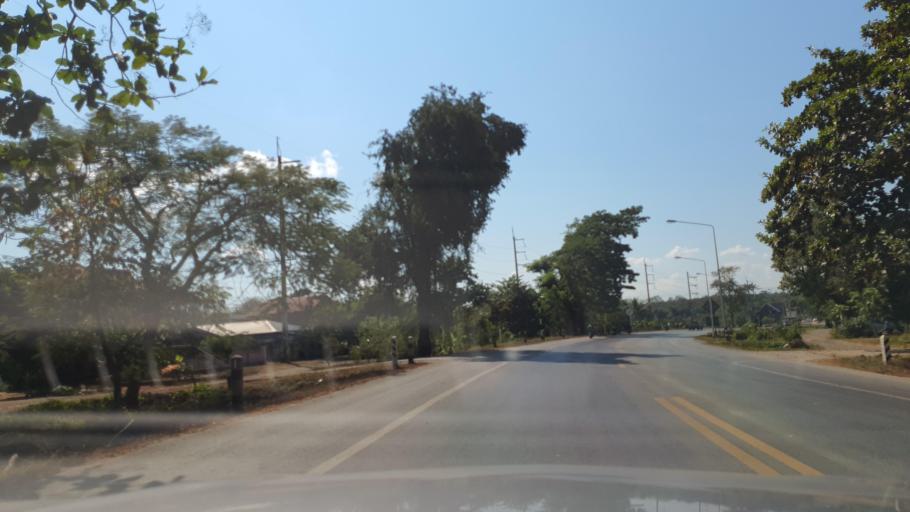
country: TH
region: Nan
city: Tha Wang Pha
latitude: 19.0257
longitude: 100.7973
